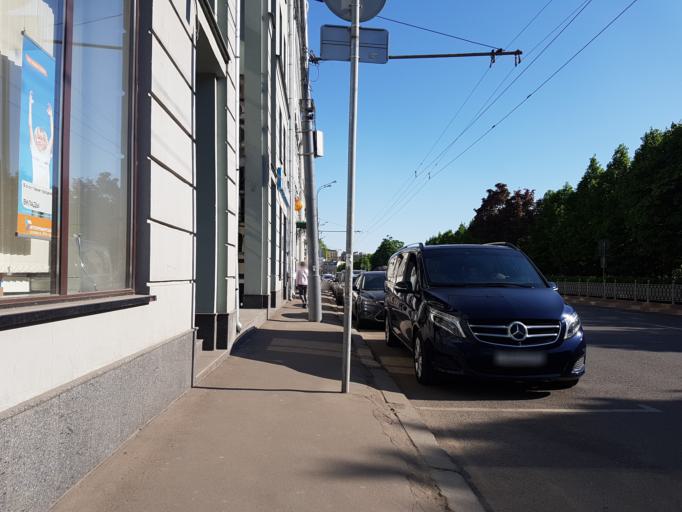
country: RU
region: Moscow
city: Moscow
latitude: 55.7722
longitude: 37.6220
